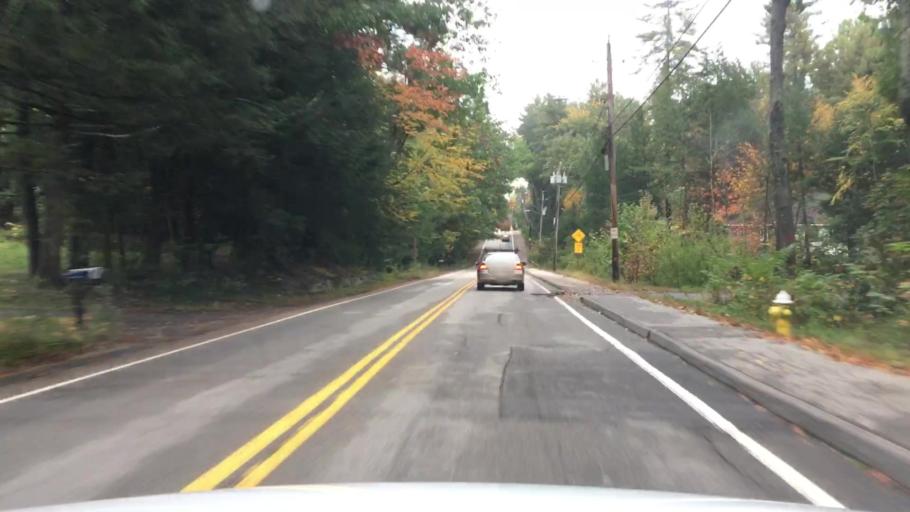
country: US
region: New Hampshire
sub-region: Strafford County
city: Durham
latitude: 43.1469
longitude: -70.9287
